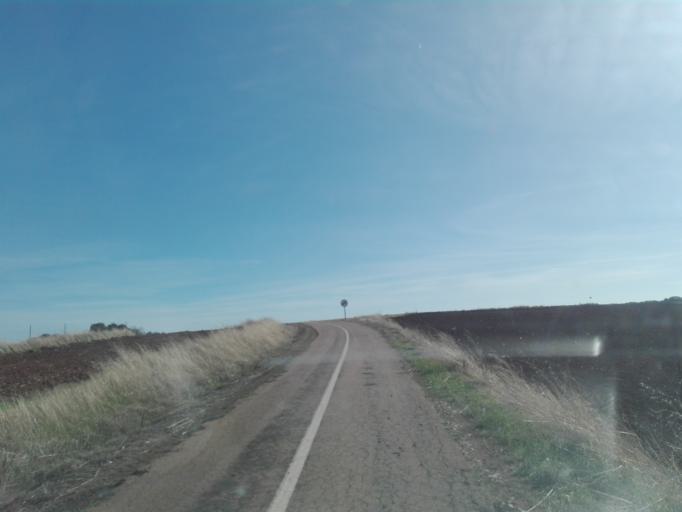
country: ES
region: Extremadura
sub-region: Provincia de Badajoz
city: Valencia de las Torres
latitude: 38.3272
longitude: -5.9497
